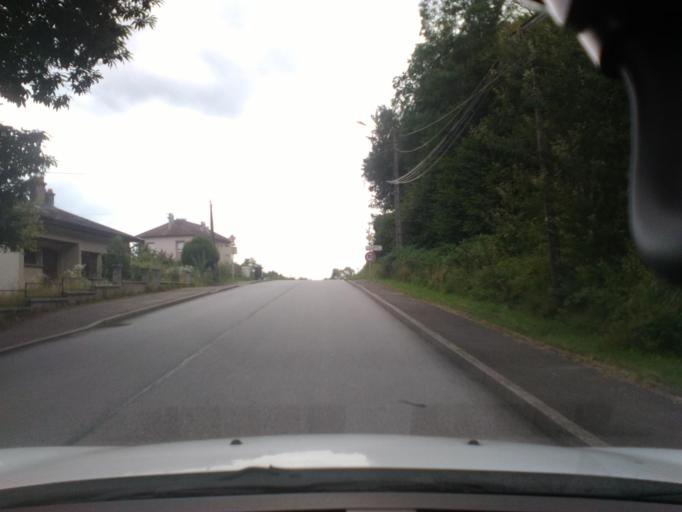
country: FR
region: Lorraine
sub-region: Departement des Vosges
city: Docelles
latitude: 48.1698
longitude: 6.6622
